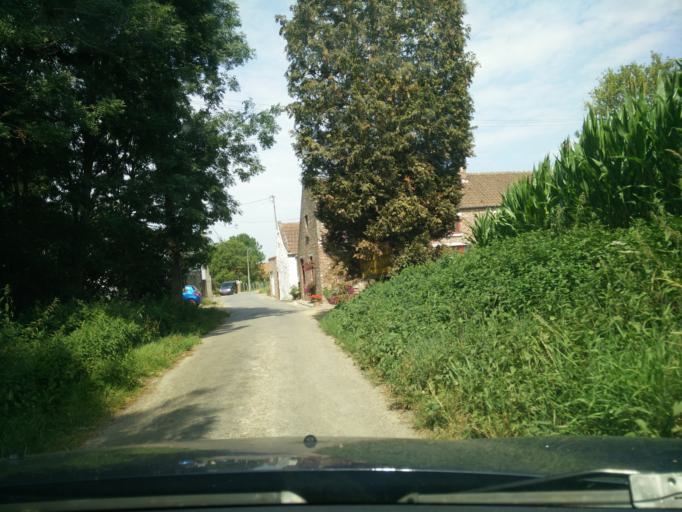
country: BE
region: Wallonia
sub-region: Province du Brabant Wallon
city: Tubize
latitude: 50.6536
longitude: 4.1944
